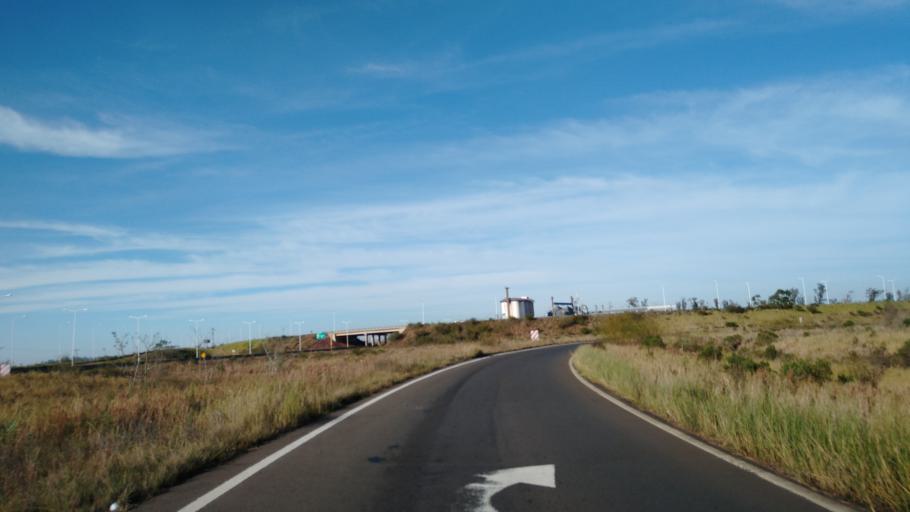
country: AR
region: Corrientes
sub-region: Departamento de Paso de los Libres
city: Paso de los Libres
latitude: -29.7091
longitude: -57.2091
